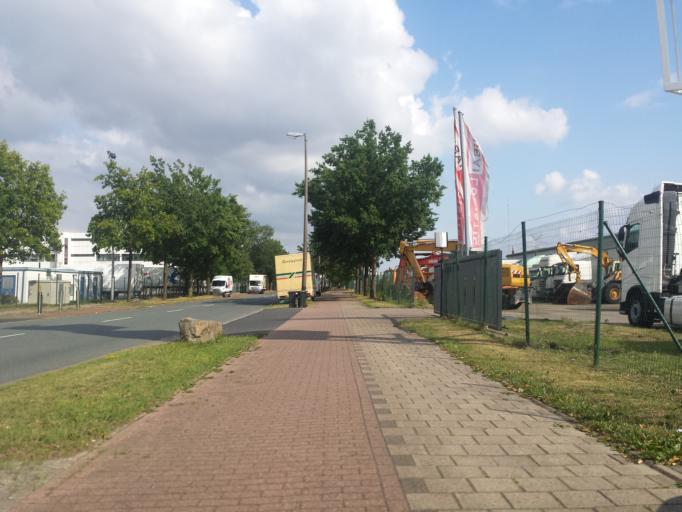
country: DE
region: Lower Saxony
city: Stuhr
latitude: 53.0843
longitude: 8.7211
